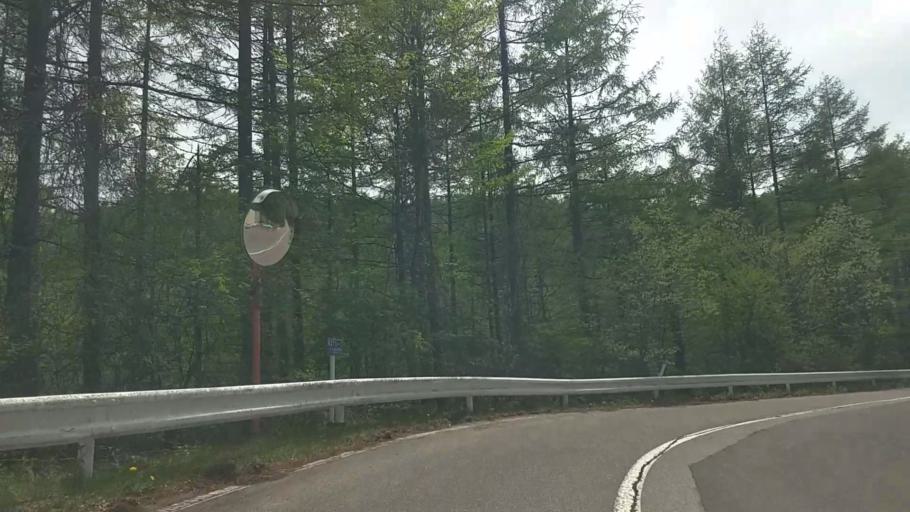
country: JP
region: Nagano
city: Saku
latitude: 36.0931
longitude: 138.3874
